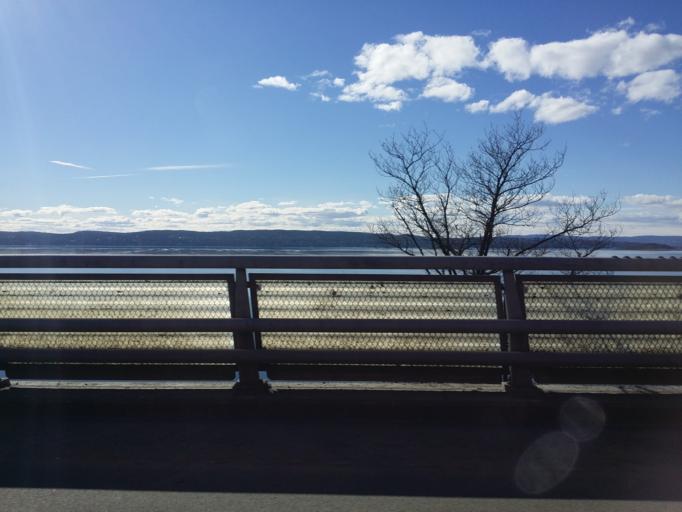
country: NO
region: Akershus
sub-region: Oppegard
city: Kolbotn
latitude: 59.8575
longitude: 10.7847
